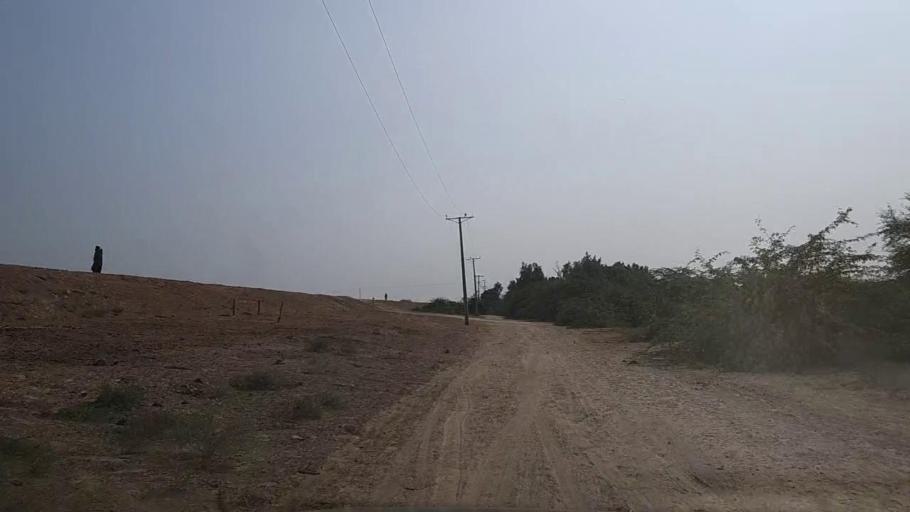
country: PK
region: Sindh
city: Chuhar Jamali
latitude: 24.5535
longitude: 67.9173
